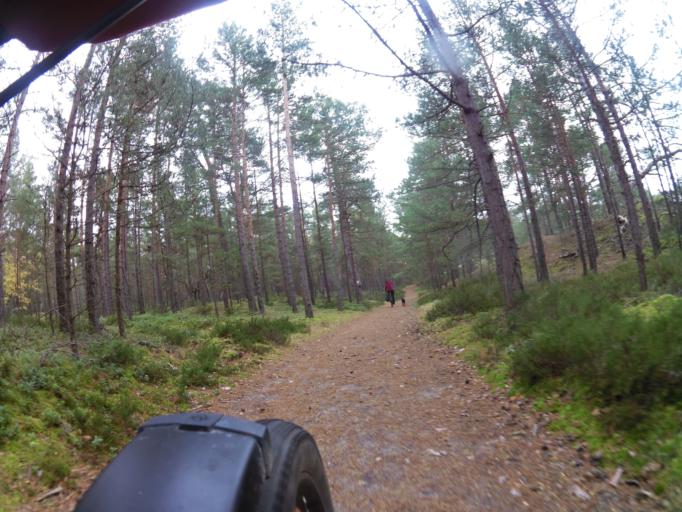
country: PL
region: Pomeranian Voivodeship
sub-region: Powiat pucki
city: Hel
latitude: 54.6253
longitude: 18.8035
